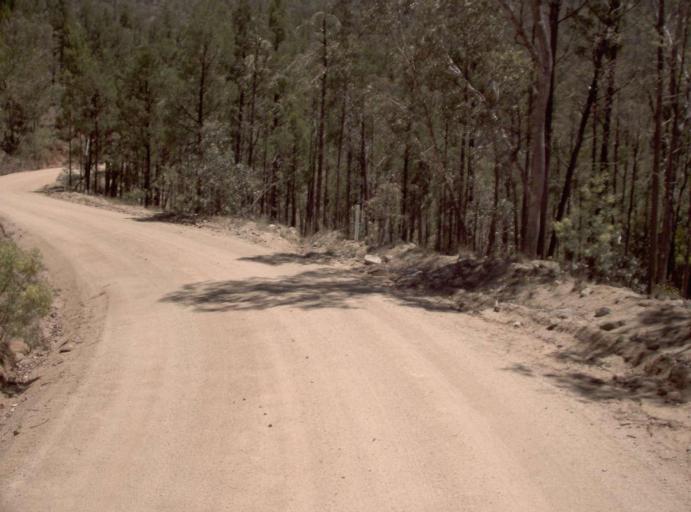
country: AU
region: New South Wales
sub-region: Snowy River
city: Jindabyne
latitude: -36.9048
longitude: 148.4170
